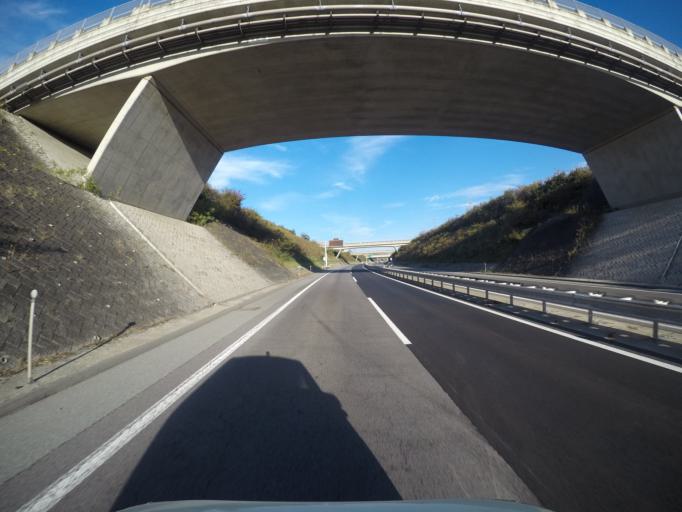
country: JP
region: Nagano
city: Komoro
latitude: 36.2827
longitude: 138.4876
